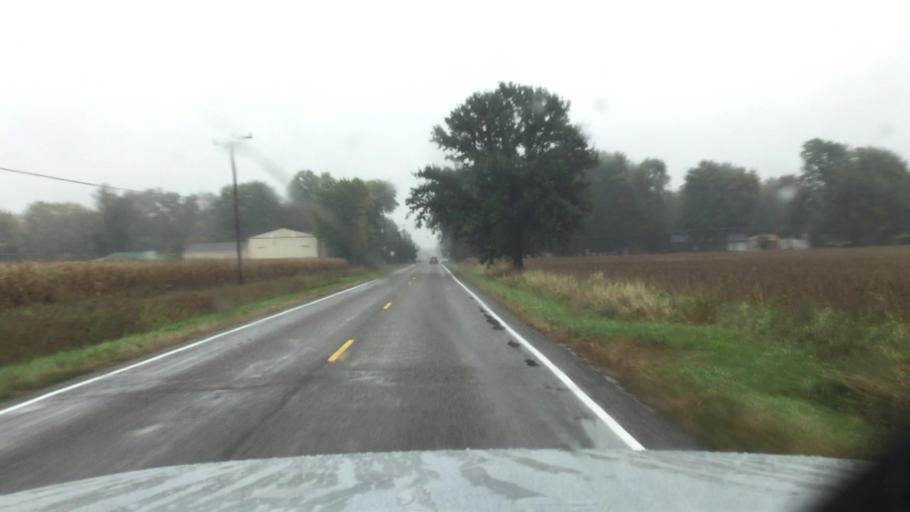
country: US
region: Michigan
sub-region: Saginaw County
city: Bridgeport
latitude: 43.3510
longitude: -83.9473
